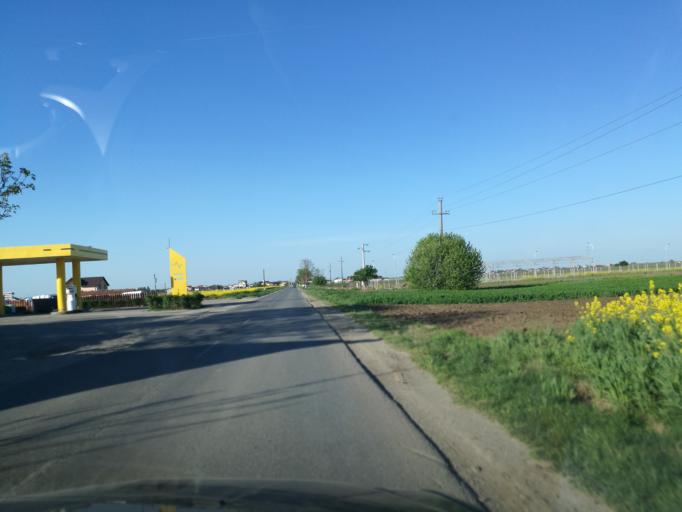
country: RO
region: Ilfov
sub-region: Comuna Vidra
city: Vidra
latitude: 44.2834
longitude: 26.1808
